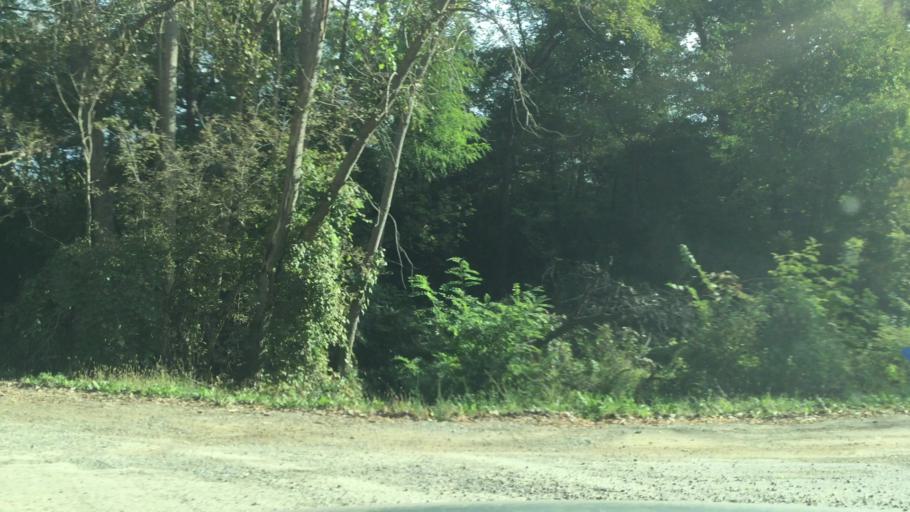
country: US
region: Michigan
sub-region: Livingston County
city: Howell
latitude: 42.6008
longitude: -83.8648
